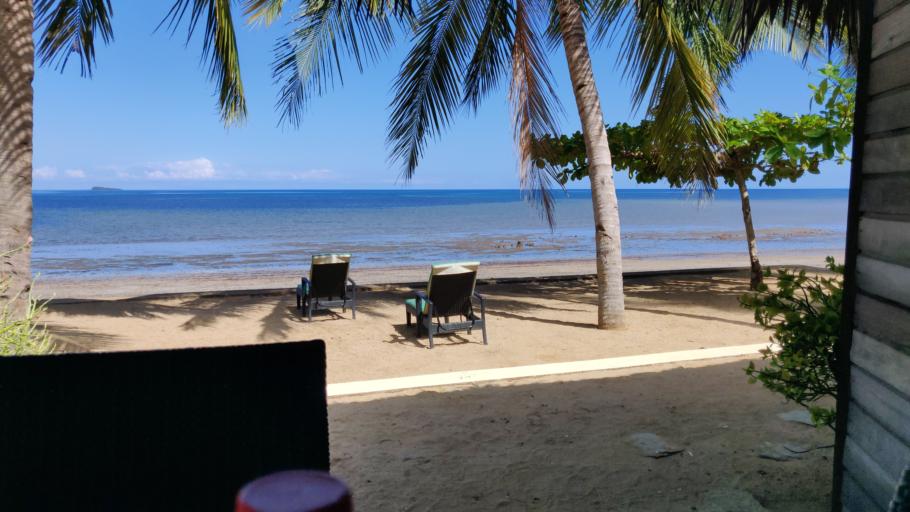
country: MG
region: Diana
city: Hell-Ville
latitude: -13.2419
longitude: 48.2533
